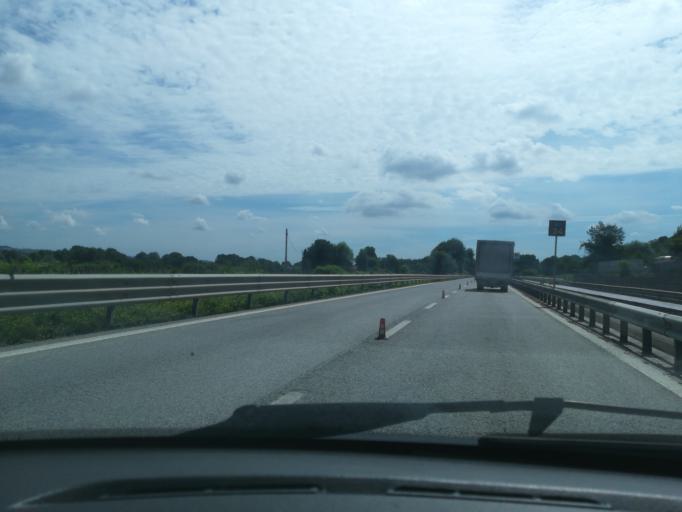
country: IT
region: The Marches
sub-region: Provincia di Macerata
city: Zona Industriale
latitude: 43.2693
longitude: 13.5064
